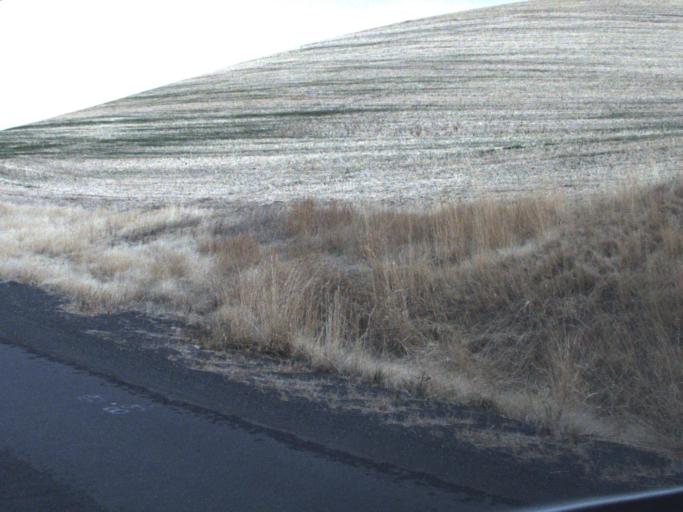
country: US
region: Washington
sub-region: Asotin County
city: Clarkston
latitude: 46.4859
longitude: -117.0694
